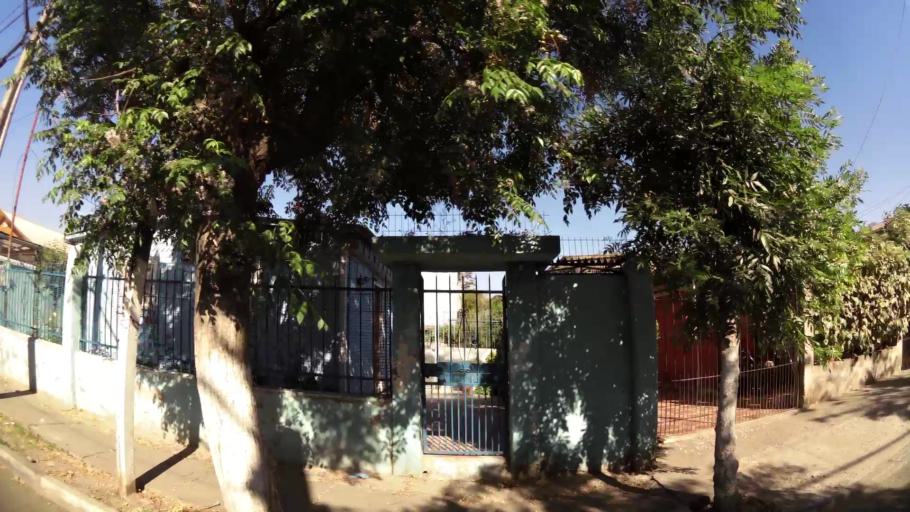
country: CL
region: Santiago Metropolitan
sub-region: Provincia de Maipo
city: San Bernardo
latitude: -33.5505
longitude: -70.6876
